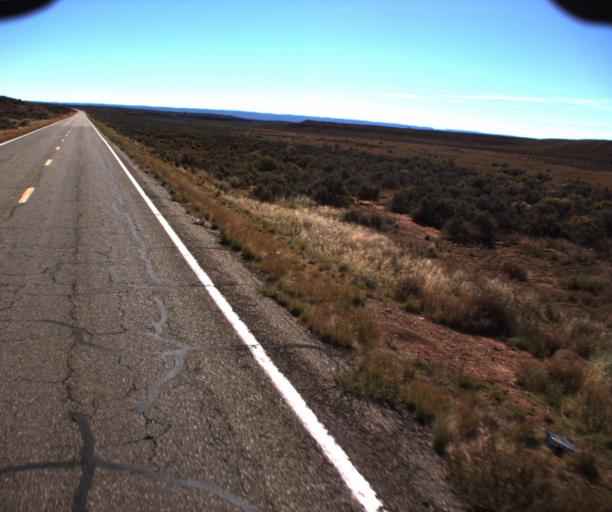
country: US
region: Arizona
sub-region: Coconino County
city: Fredonia
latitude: 36.9145
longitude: -112.4251
